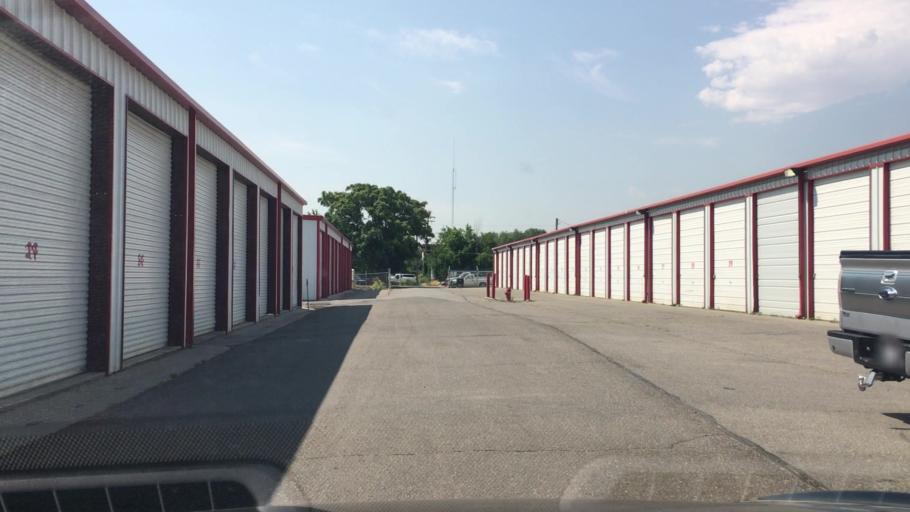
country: US
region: Utah
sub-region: Salt Lake County
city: Millcreek
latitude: 40.6811
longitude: -111.8860
